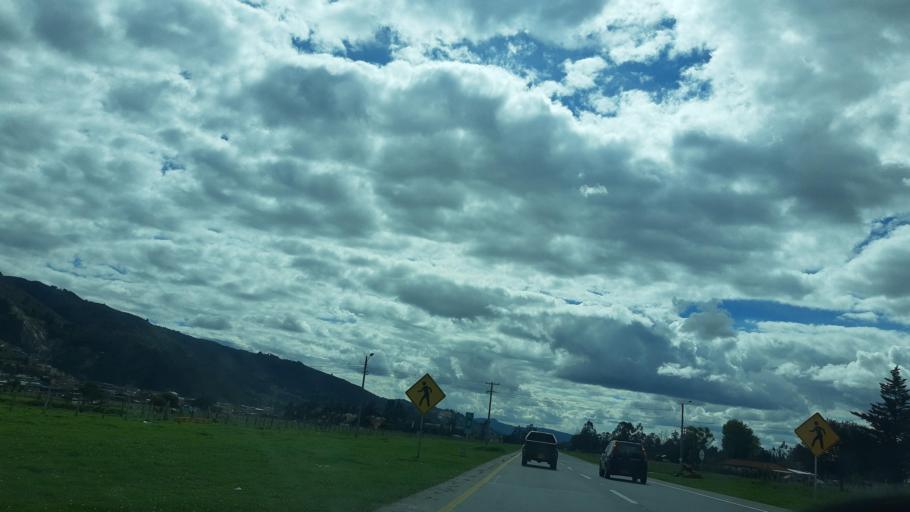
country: CO
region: Cundinamarca
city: Gachancipa
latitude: 4.9979
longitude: -73.8719
